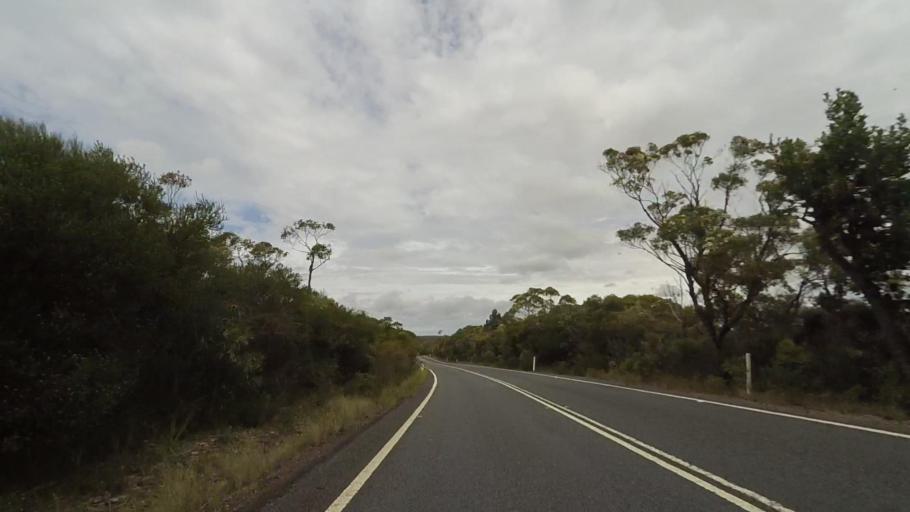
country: AU
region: New South Wales
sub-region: Sutherland Shire
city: Heathcote
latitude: -34.1091
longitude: 151.0598
